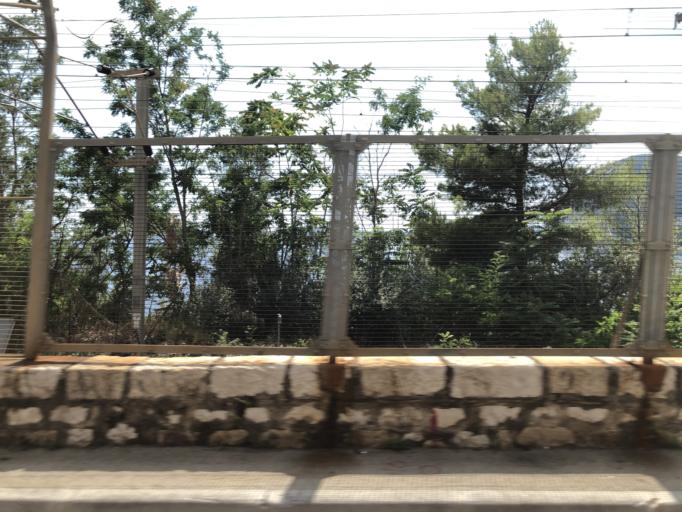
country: FR
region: Provence-Alpes-Cote d'Azur
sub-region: Departement des Alpes-Maritimes
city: Eze
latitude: 43.7221
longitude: 7.3656
